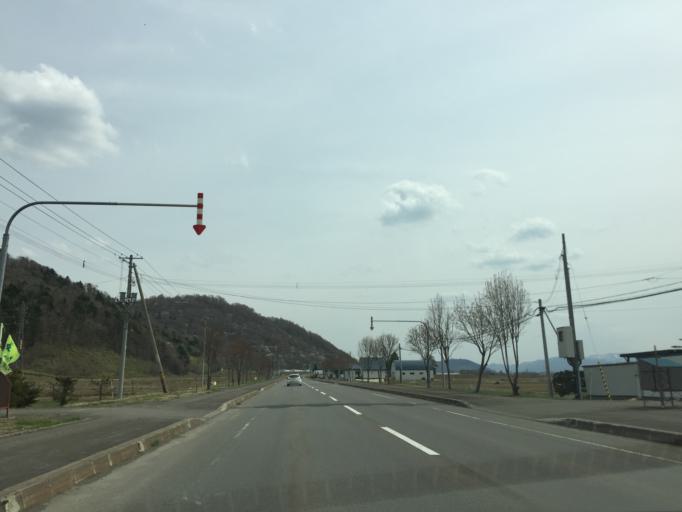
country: JP
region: Hokkaido
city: Ashibetsu
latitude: 43.5418
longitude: 142.1616
